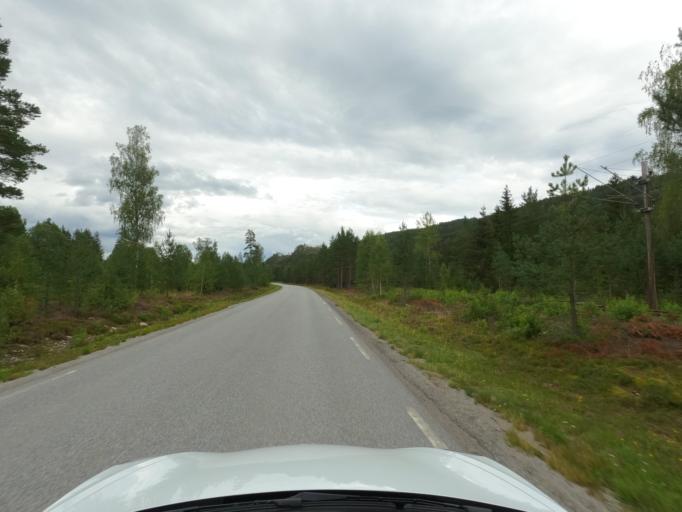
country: NO
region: Telemark
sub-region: Hjartdal
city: Sauland
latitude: 59.6943
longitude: 9.0656
